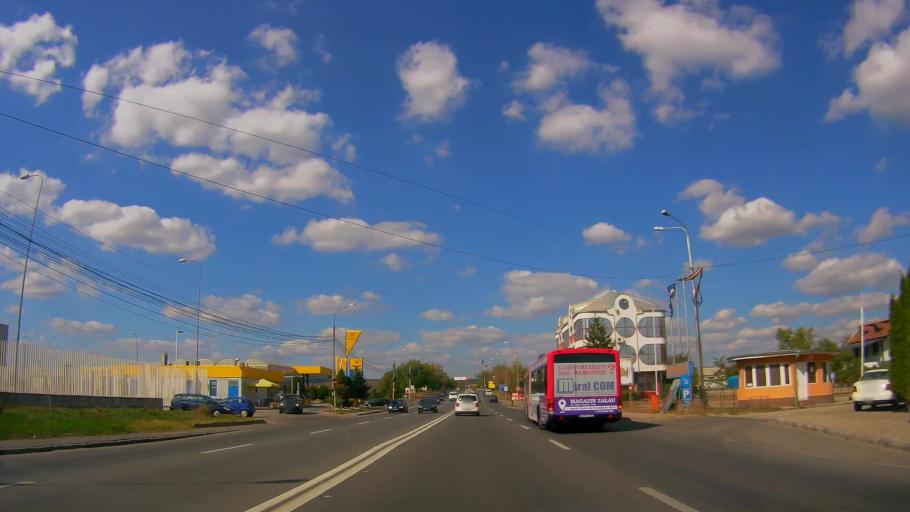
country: RO
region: Salaj
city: Zalau
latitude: 47.2144
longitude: 23.0427
